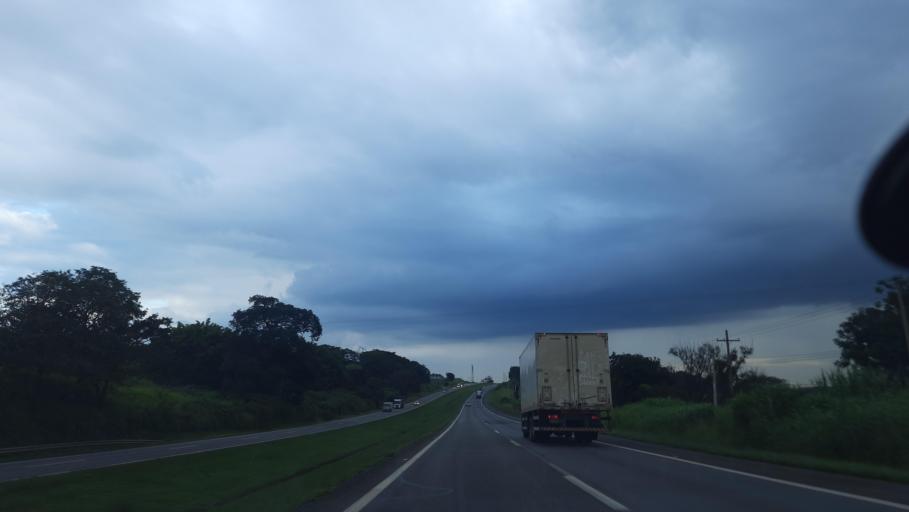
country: BR
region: Sao Paulo
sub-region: Mogi-Mirim
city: Mogi Mirim
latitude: -22.4971
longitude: -46.9835
